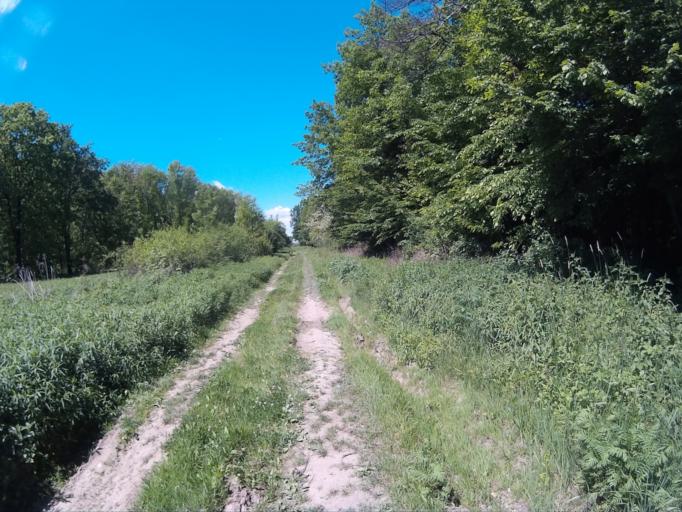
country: HU
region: Vas
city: Kormend
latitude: 46.9714
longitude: 16.5883
